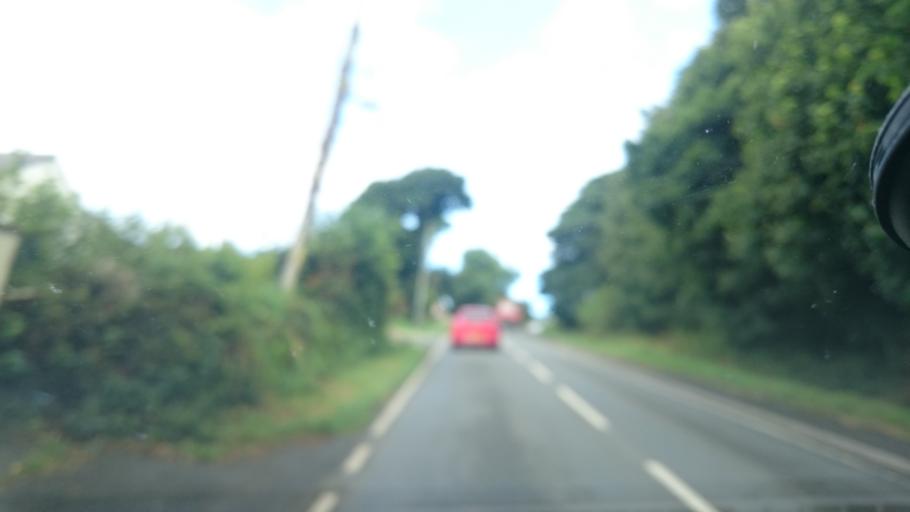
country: GB
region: Wales
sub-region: Pembrokeshire
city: Freystrop
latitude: 51.7624
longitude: -4.9604
